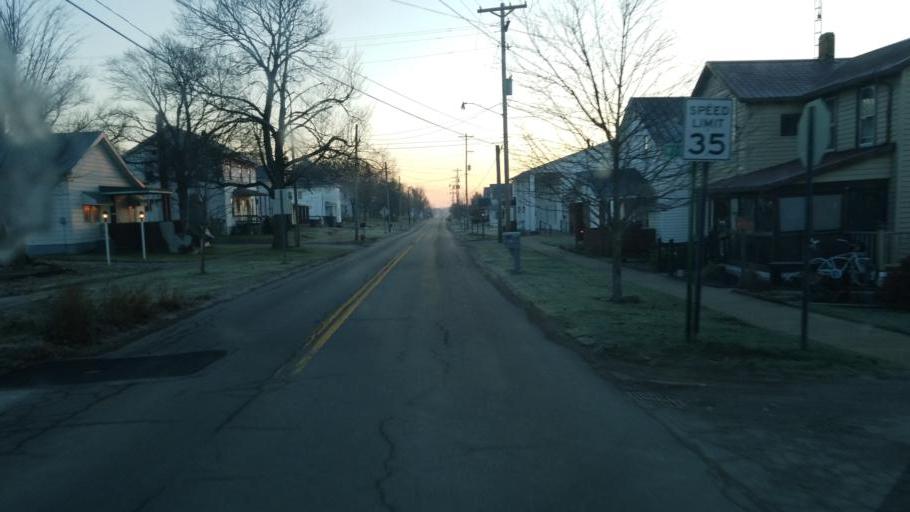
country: US
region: Ohio
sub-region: Wayne County
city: West Salem
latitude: 40.9716
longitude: -82.1090
